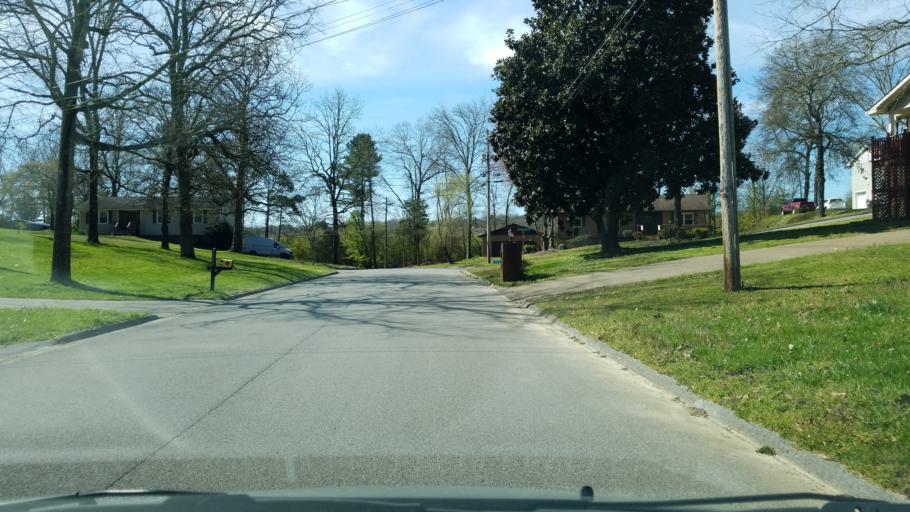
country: US
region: Tennessee
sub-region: Hamilton County
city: Collegedale
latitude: 35.0833
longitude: -85.0882
